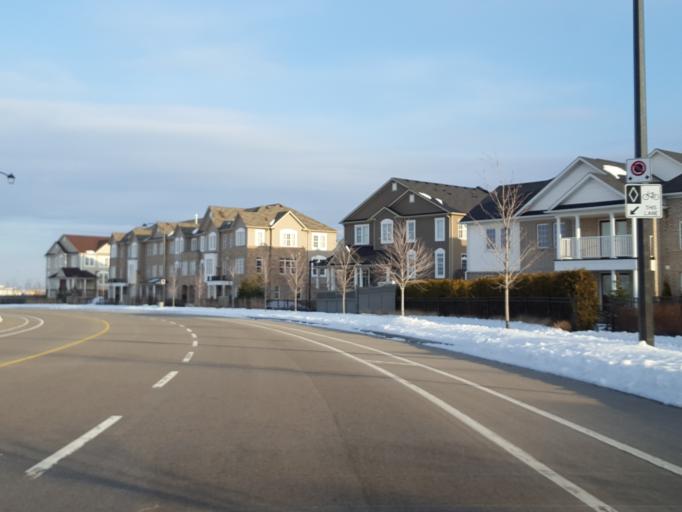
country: CA
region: Ontario
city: Burlington
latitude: 43.4106
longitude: -79.8195
